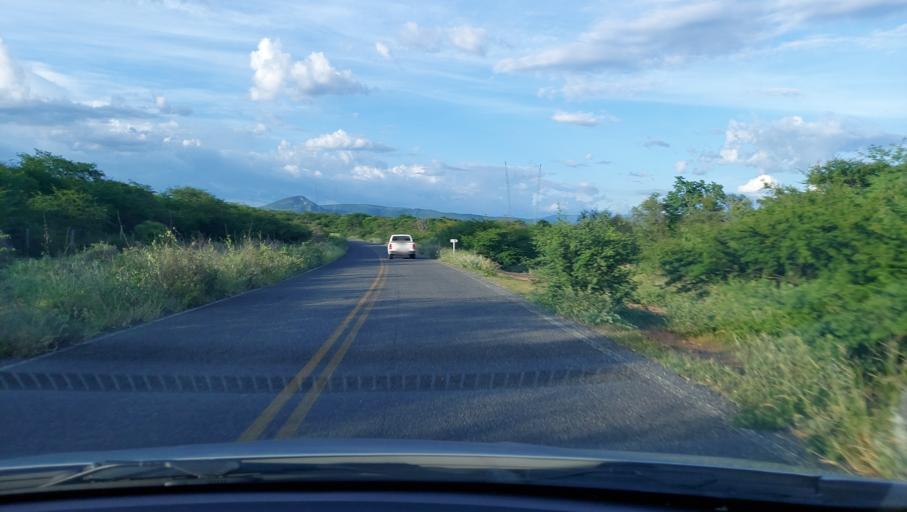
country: BR
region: Bahia
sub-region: Oliveira Dos Brejinhos
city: Beira Rio
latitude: -12.1954
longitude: -42.5376
